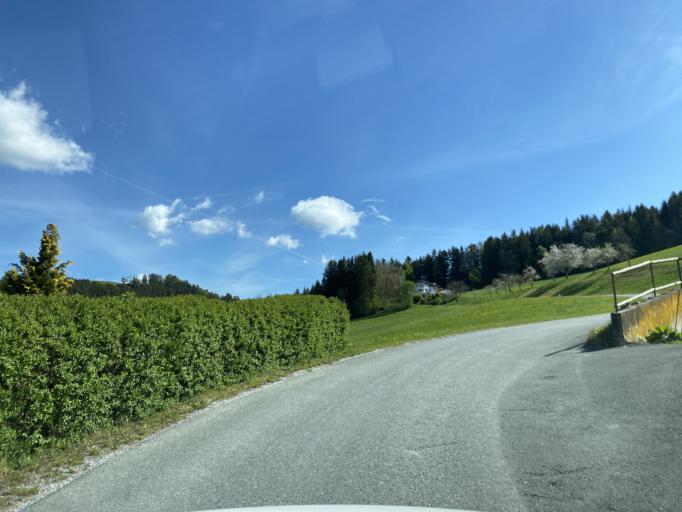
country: AT
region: Styria
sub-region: Politischer Bezirk Weiz
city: Birkfeld
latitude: 47.3678
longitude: 15.6958
